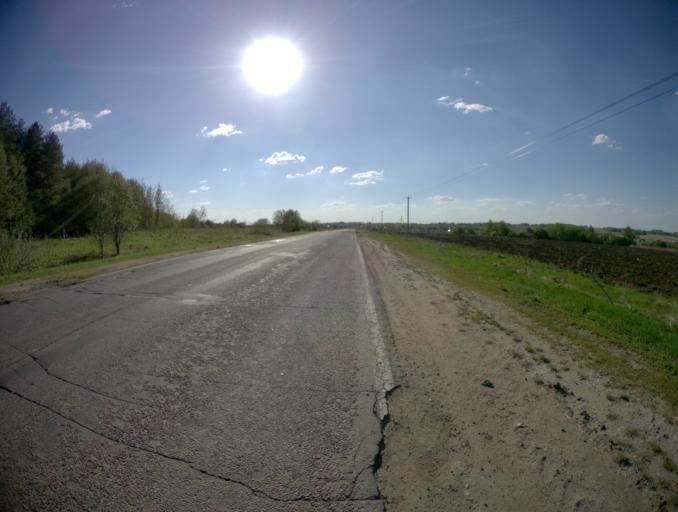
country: RU
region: Ivanovo
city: Gavrilov Posad
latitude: 56.3461
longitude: 40.1668
